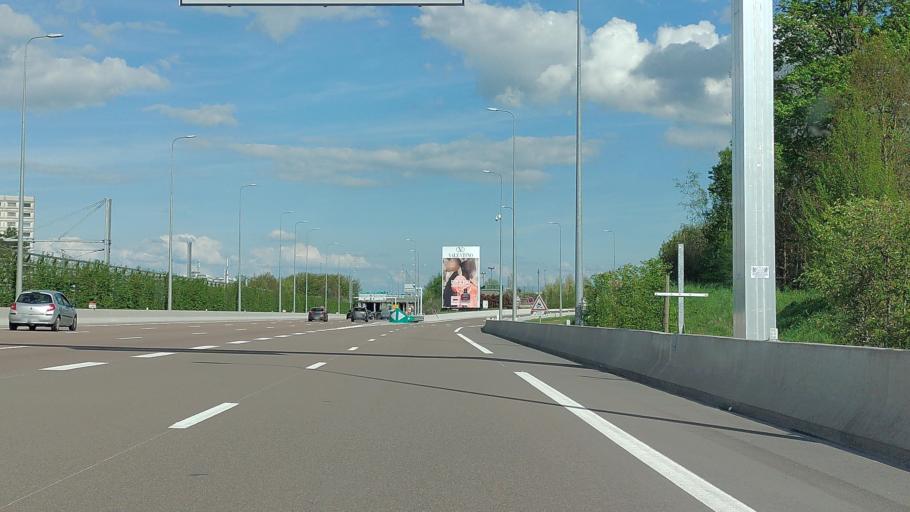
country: FR
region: Ile-de-France
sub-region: Departement du Val-d'Oise
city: Roissy-en-France
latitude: 49.0054
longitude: 2.5434
